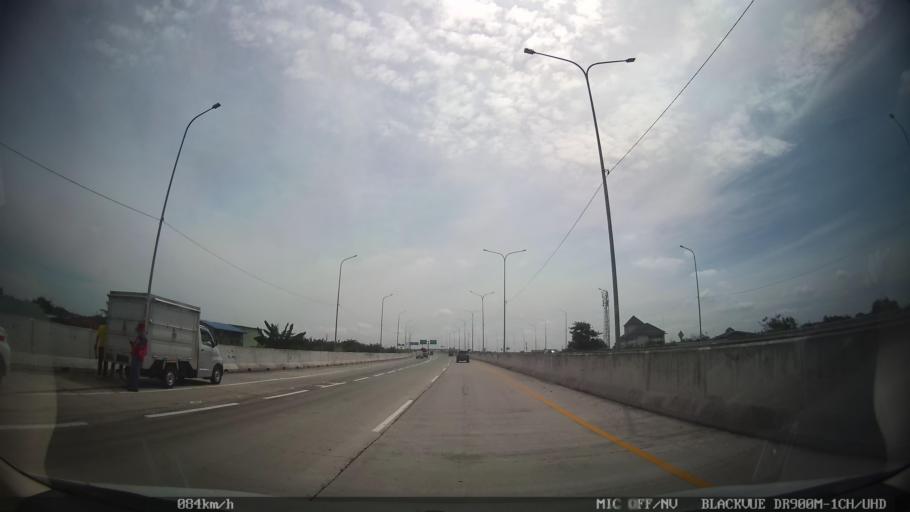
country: ID
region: North Sumatra
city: Medan
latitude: 3.6478
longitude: 98.6743
